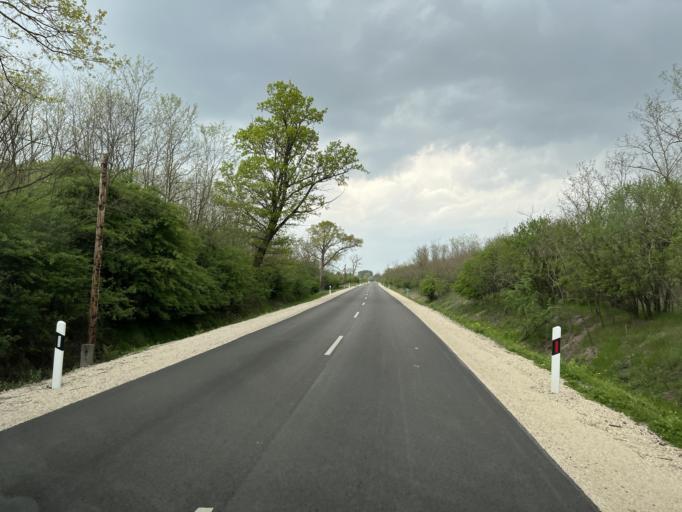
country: HU
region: Pest
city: Csemo
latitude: 47.0604
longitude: 19.7115
